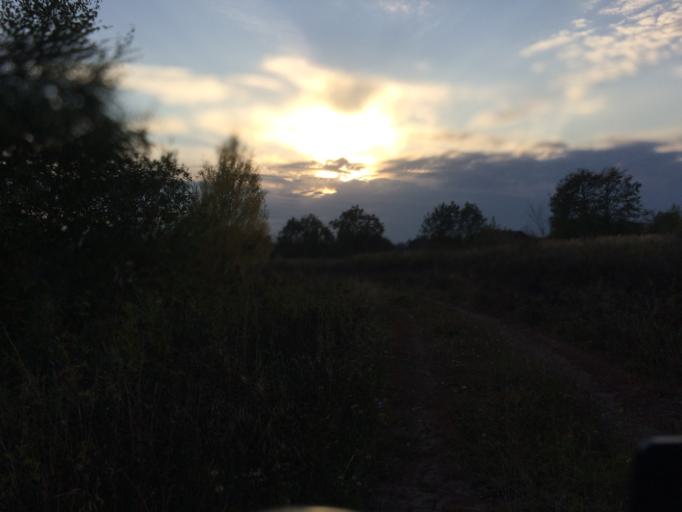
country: RU
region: Mariy-El
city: Yoshkar-Ola
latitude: 56.6475
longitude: 47.9212
